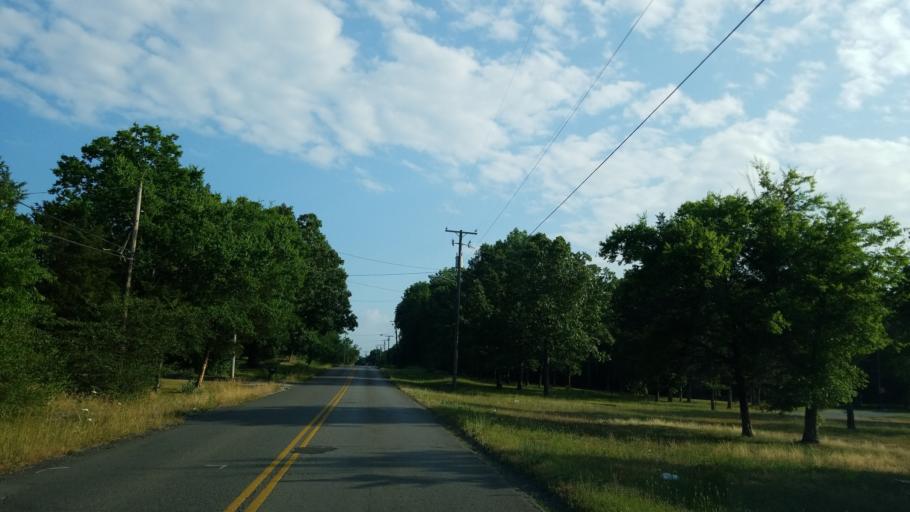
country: US
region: Tennessee
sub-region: Rutherford County
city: La Vergne
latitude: 36.0427
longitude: -86.5853
